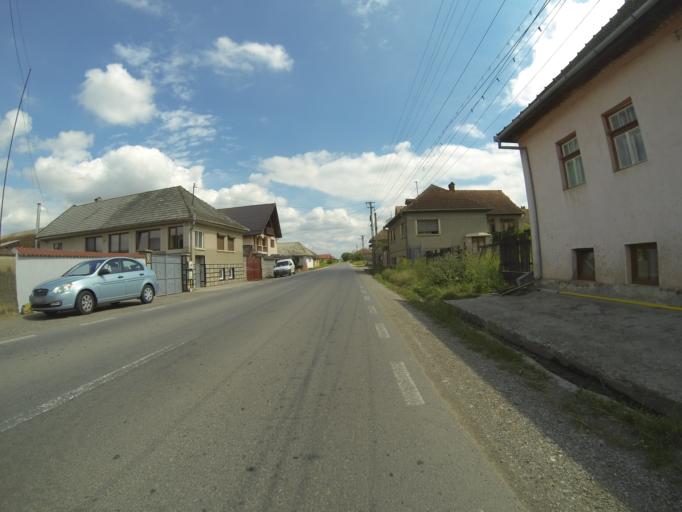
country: RO
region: Brasov
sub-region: Comuna Hoghiz
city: Hoghiz
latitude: 45.9691
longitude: 25.2996
